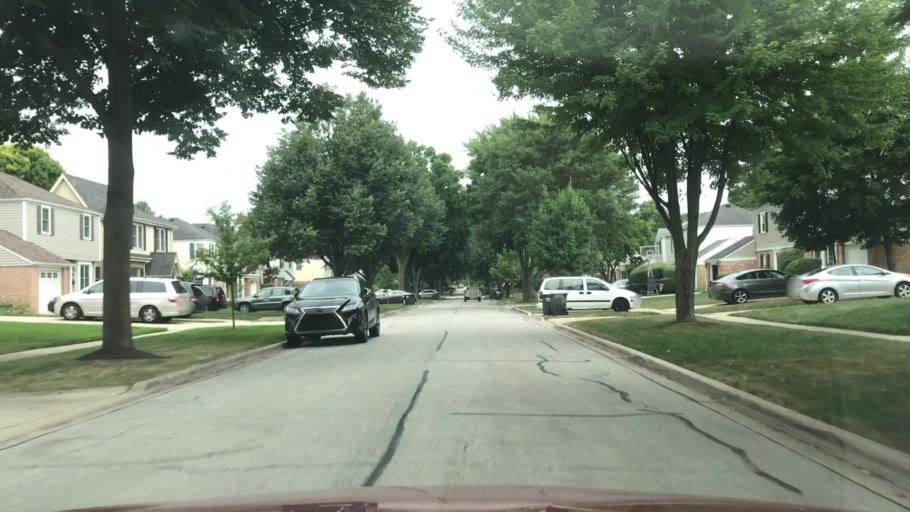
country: US
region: Illinois
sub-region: Cook County
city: Arlington Heights
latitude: 42.0719
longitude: -87.9879
